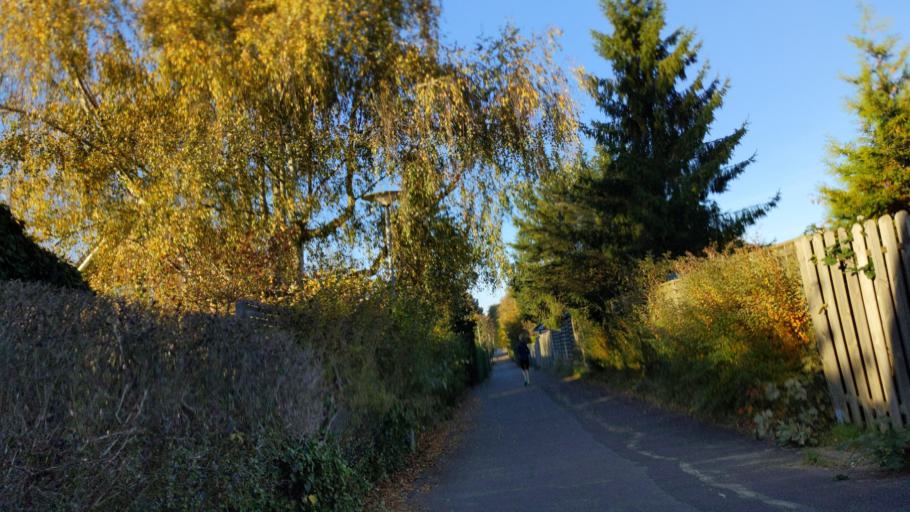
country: DE
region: Schleswig-Holstein
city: Gross Gronau
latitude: 53.8434
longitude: 10.7383
